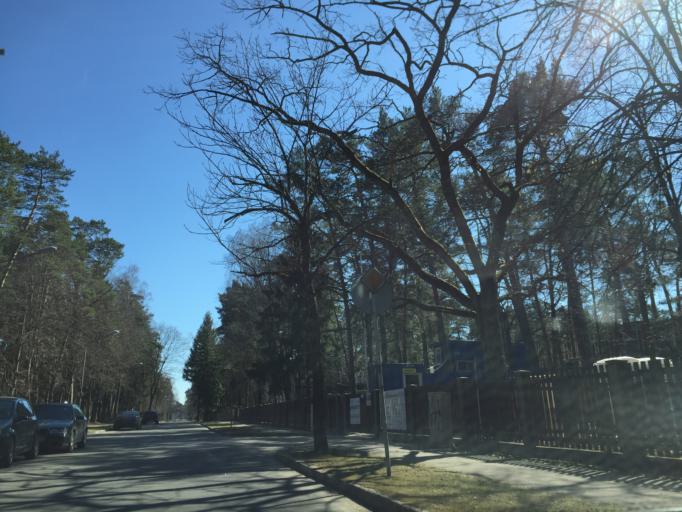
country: LV
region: Babite
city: Pinki
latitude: 56.9861
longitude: 23.8779
